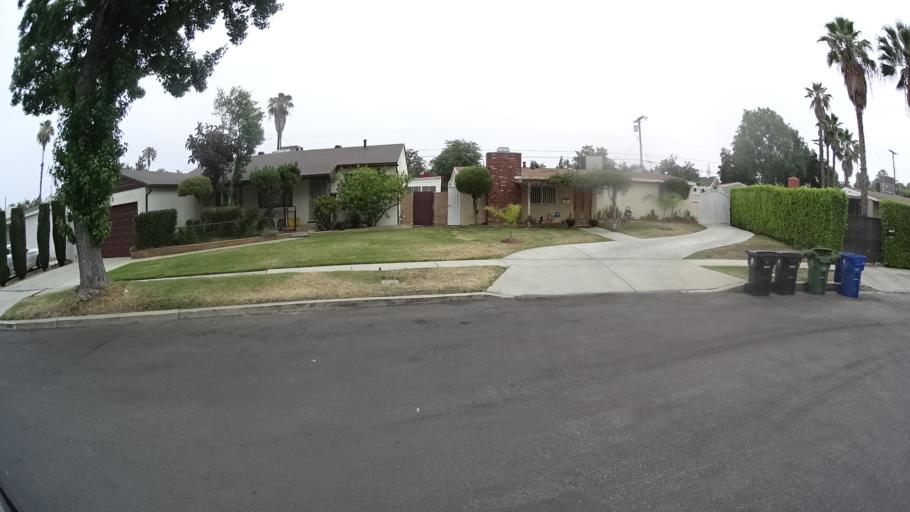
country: US
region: California
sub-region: Los Angeles County
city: Van Nuys
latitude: 34.1923
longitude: -118.4191
